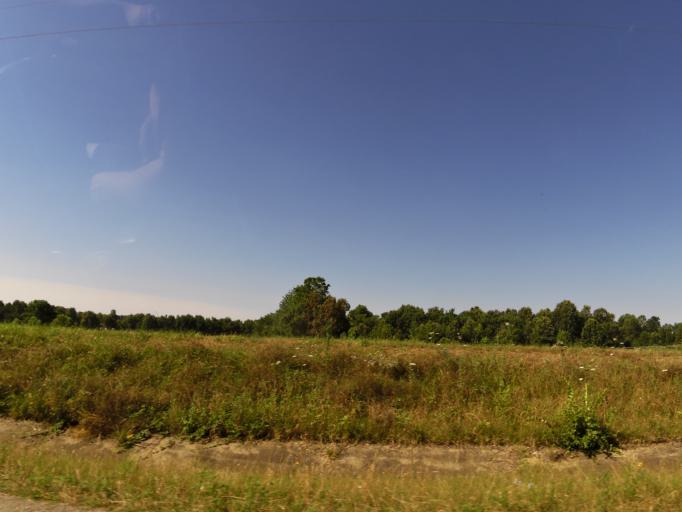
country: US
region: Arkansas
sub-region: Clay County
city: Piggott
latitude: 36.4318
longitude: -90.2980
